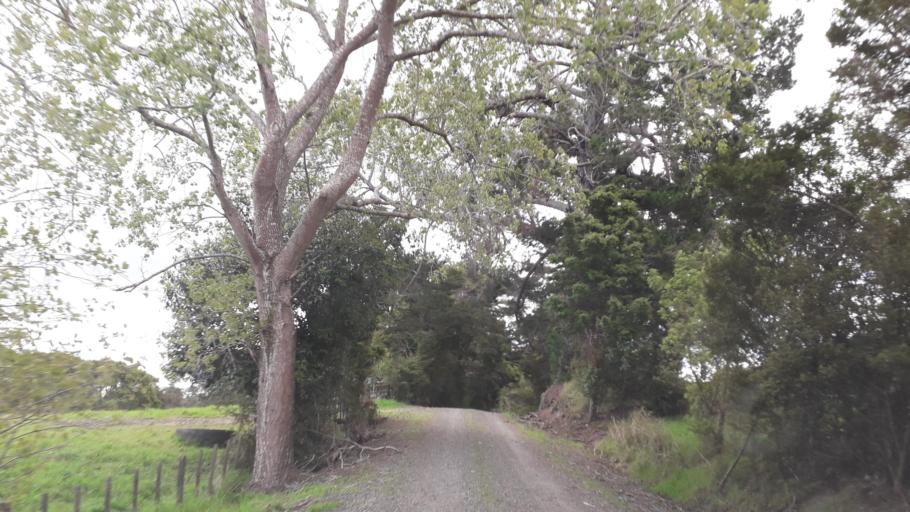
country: NZ
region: Northland
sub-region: Far North District
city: Waimate North
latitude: -35.3178
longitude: 173.5743
